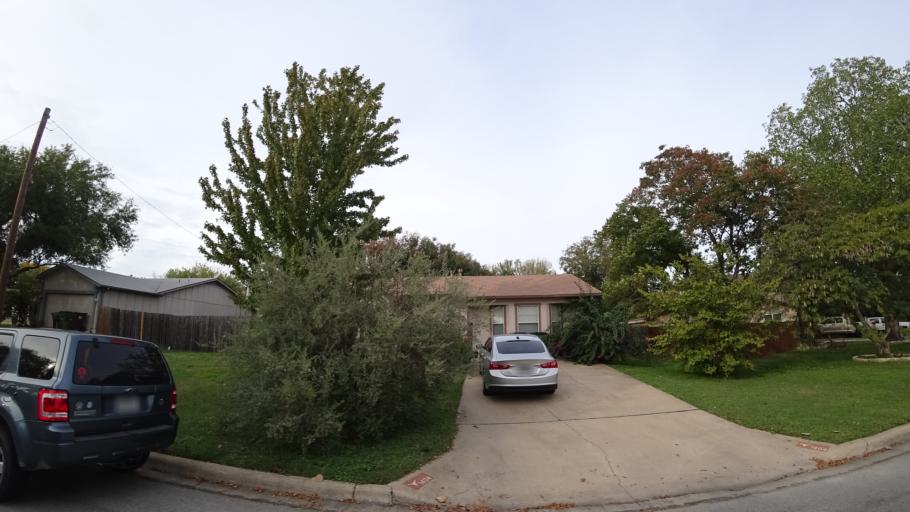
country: US
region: Texas
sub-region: Williamson County
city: Round Rock
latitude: 30.4973
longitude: -97.6638
